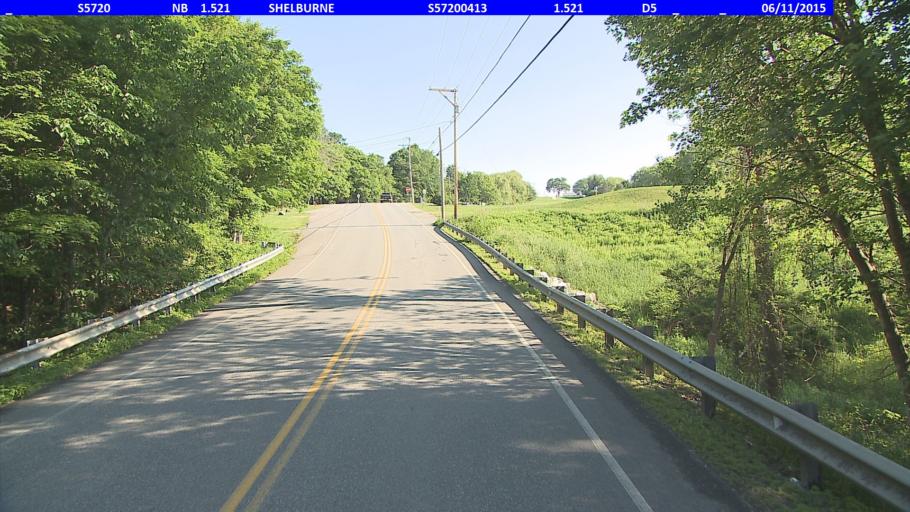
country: US
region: Vermont
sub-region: Chittenden County
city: South Burlington
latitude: 44.3898
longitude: -73.2008
